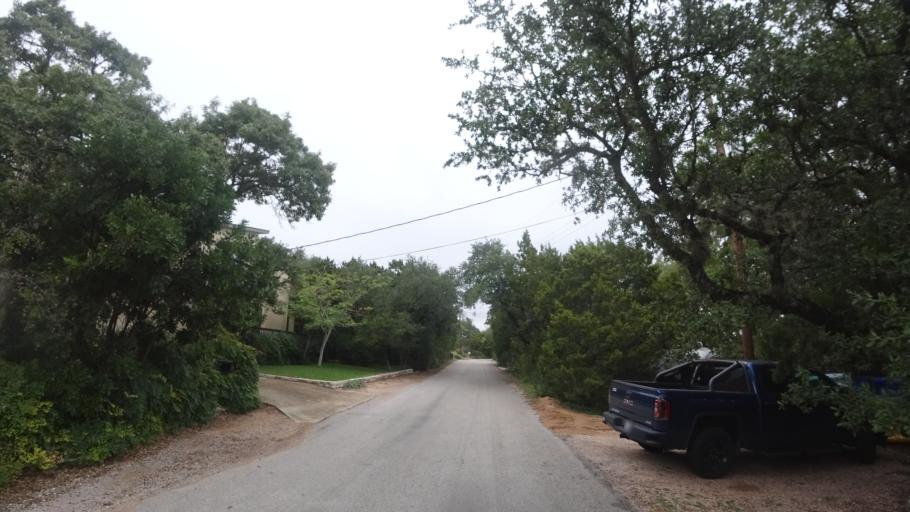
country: US
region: Texas
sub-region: Travis County
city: Hudson Bend
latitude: 30.3949
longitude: -97.9192
